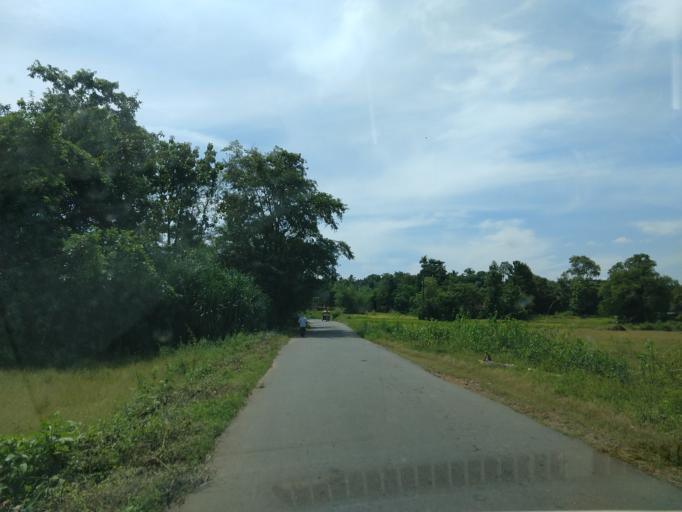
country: IN
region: Maharashtra
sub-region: Sindhudurg
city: Savantvadi
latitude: 15.9660
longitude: 73.7726
